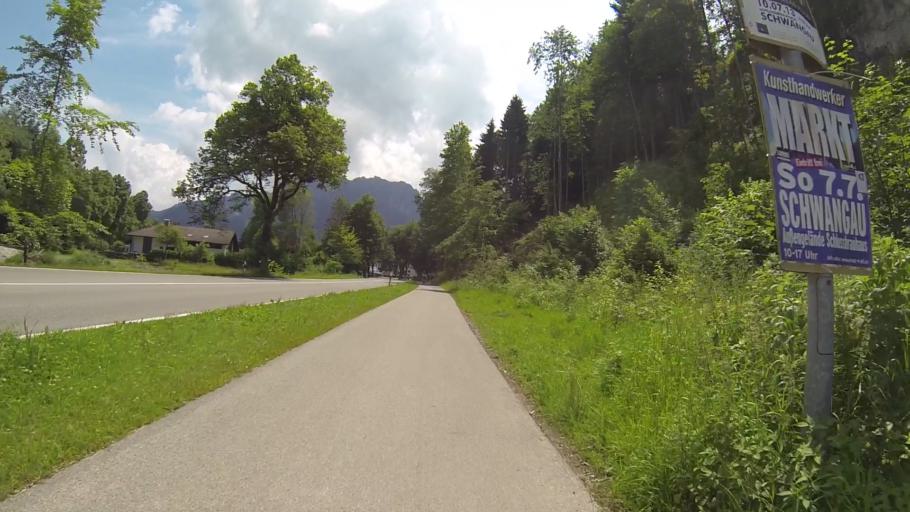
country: DE
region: Bavaria
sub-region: Swabia
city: Schwangau
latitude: 47.5660
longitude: 10.7236
